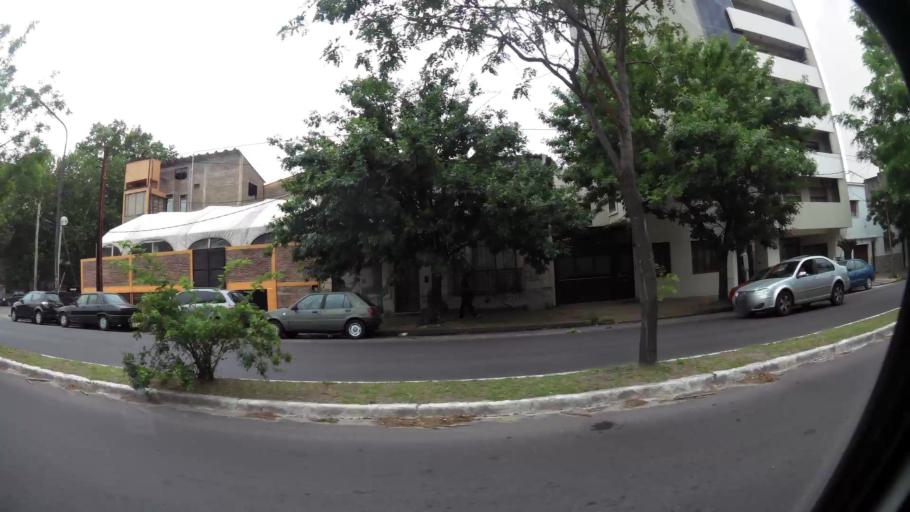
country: AR
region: Buenos Aires
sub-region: Partido de La Plata
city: La Plata
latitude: -34.9288
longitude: -57.9502
